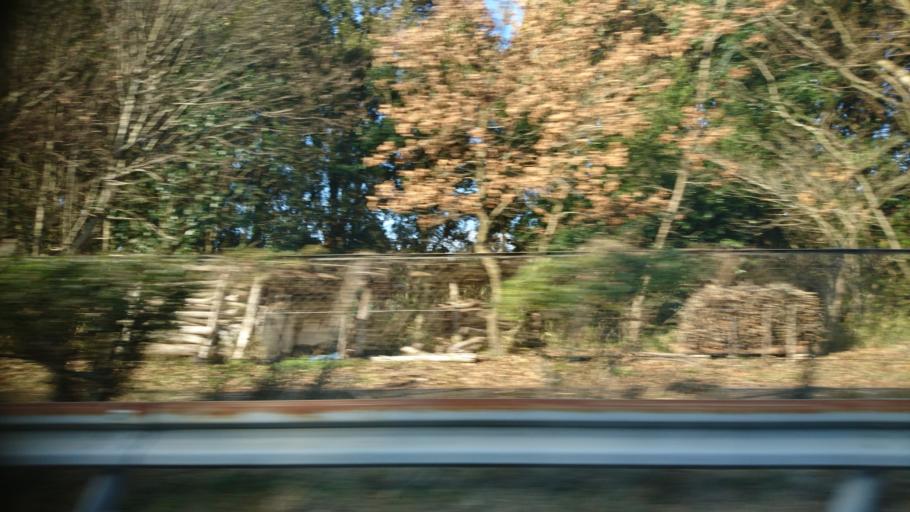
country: JP
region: Miyazaki
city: Kobayashi
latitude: 32.0263
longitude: 130.8513
